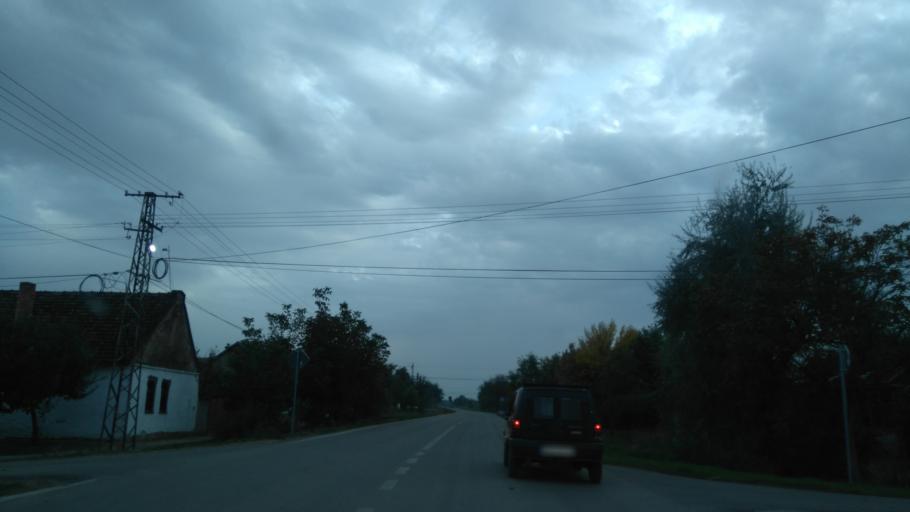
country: RS
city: Mol
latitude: 45.7626
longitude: 20.1245
